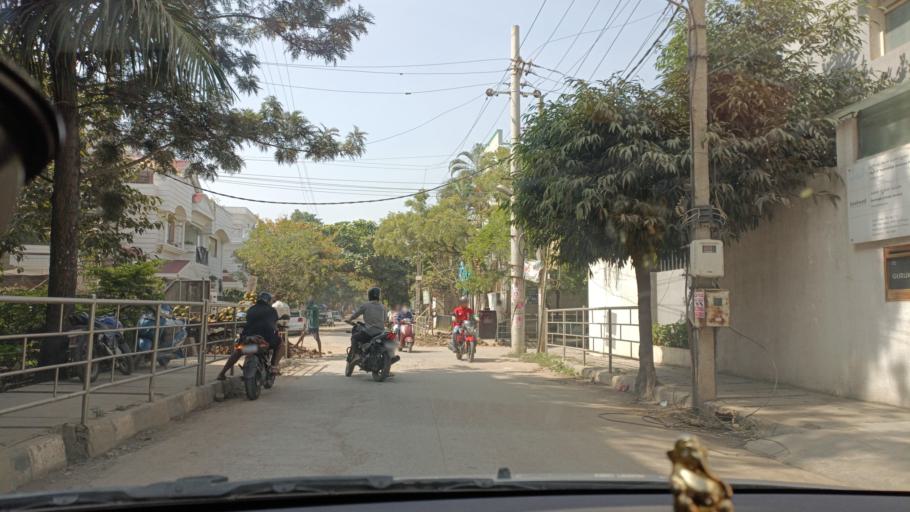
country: IN
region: Karnataka
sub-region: Bangalore Urban
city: Bangalore
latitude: 12.9181
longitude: 77.6207
